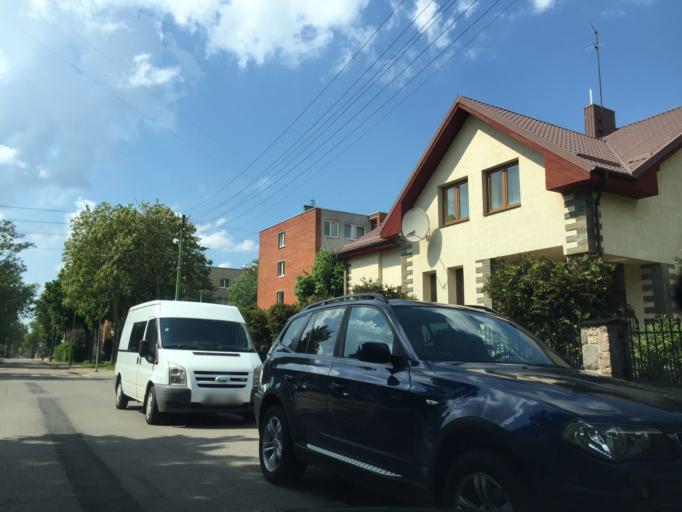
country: LT
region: Klaipedos apskritis
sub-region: Klaipeda
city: Palanga
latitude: 55.9228
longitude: 21.0723
